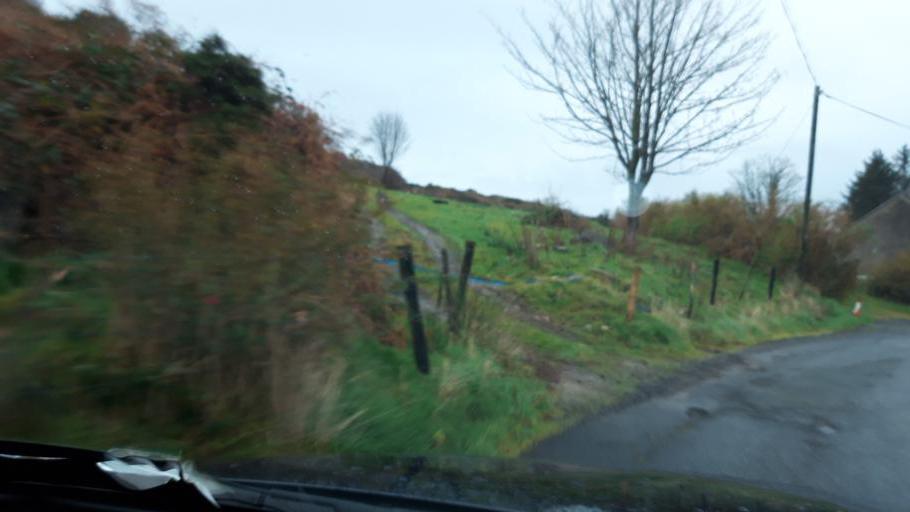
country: IE
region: Ulster
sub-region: County Donegal
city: Ramelton
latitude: 55.2289
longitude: -7.6197
